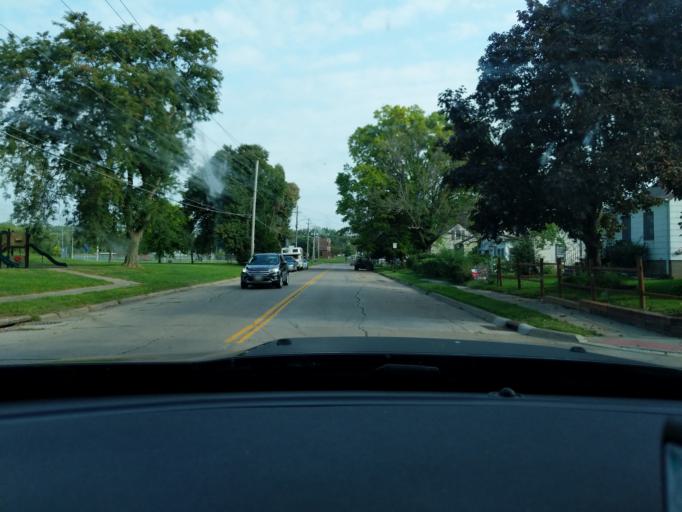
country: US
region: Illinois
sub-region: Rock Island County
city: Rock Island
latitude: 41.5039
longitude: -90.6243
